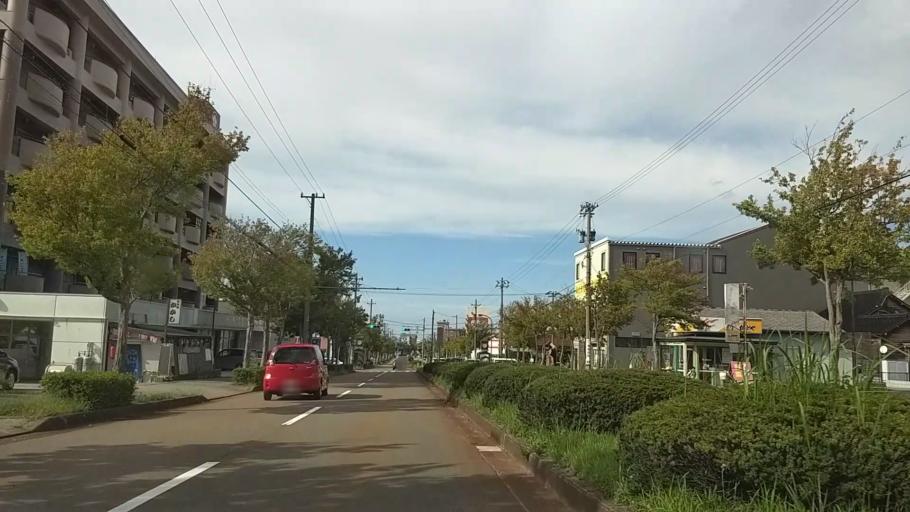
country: JP
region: Ishikawa
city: Nonoichi
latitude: 36.5251
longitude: 136.6390
